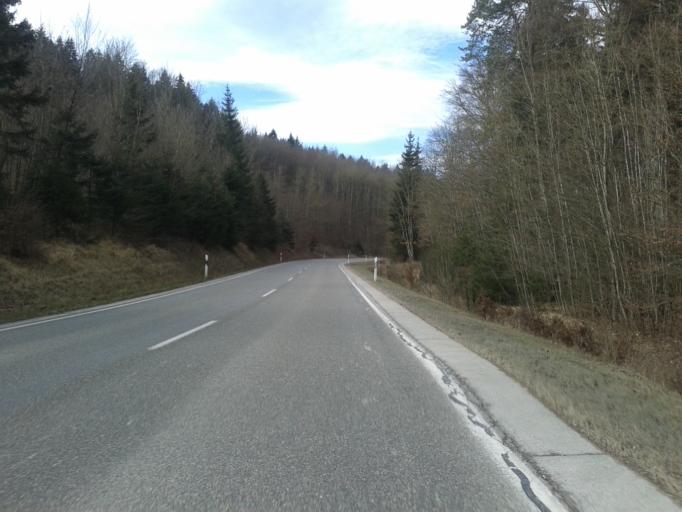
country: DE
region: Baden-Wuerttemberg
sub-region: Tuebingen Region
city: Altheim
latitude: 48.3495
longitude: 9.7828
